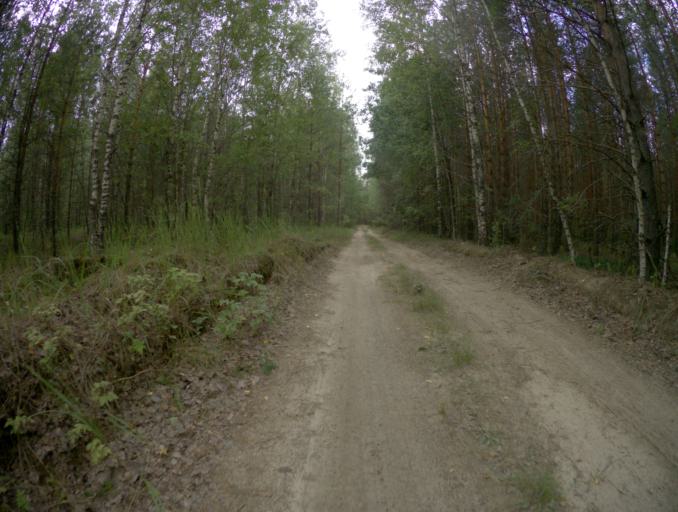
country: RU
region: Vladimir
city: Raduzhnyy
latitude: 55.9647
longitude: 40.2090
